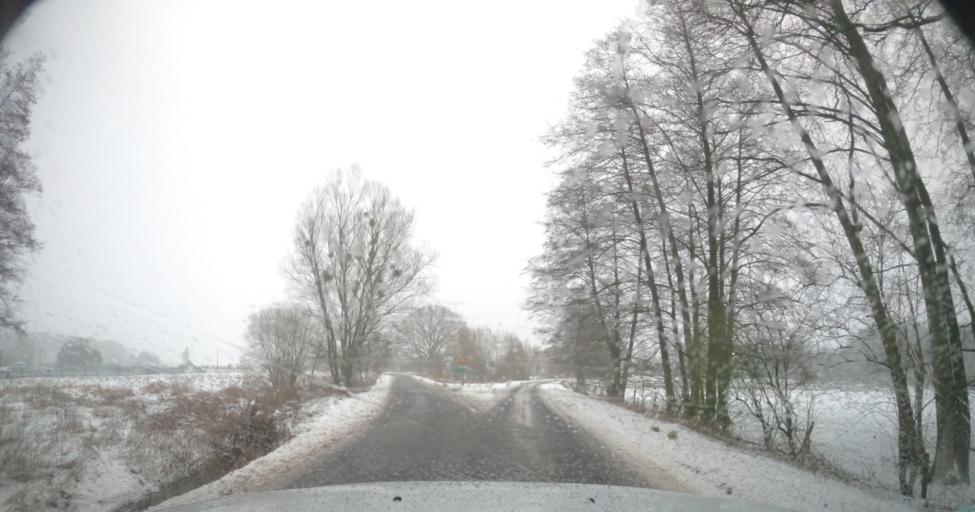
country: PL
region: West Pomeranian Voivodeship
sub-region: Powiat goleniowski
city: Przybiernow
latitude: 53.6851
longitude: 14.8402
